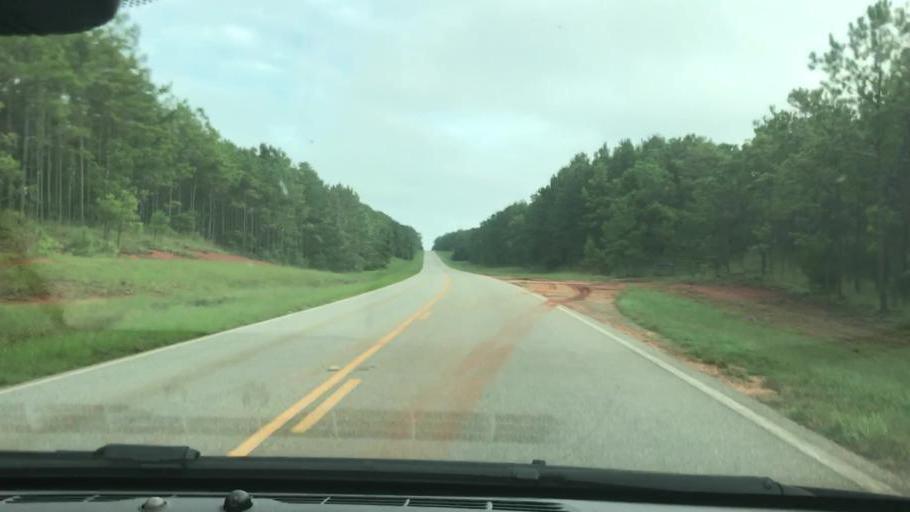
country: US
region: Georgia
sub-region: Stewart County
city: Lumpkin
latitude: 31.9929
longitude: -84.9331
